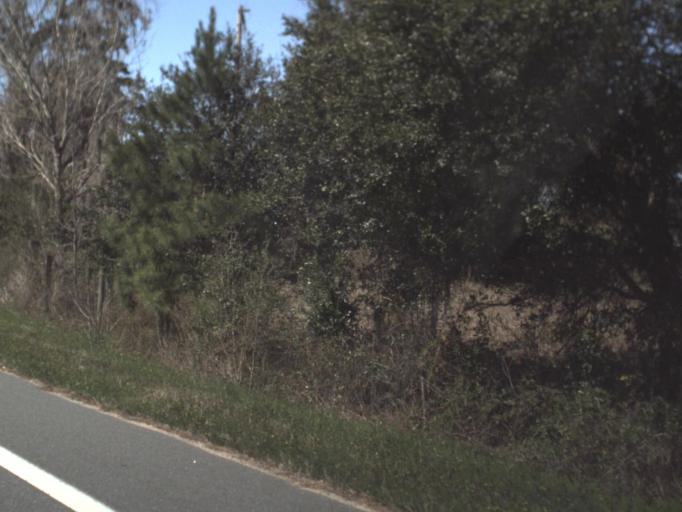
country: US
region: Florida
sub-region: Gadsden County
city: Gretna
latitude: 30.6884
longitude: -84.7220
